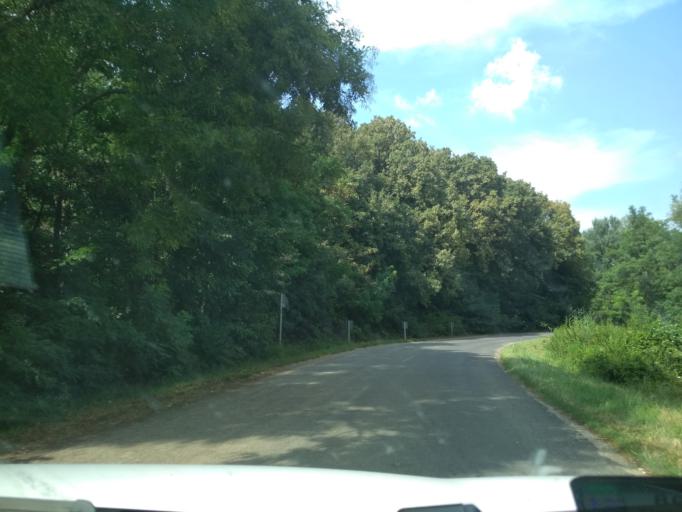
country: HU
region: Jasz-Nagykun-Szolnok
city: Tiszaszolos
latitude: 47.5281
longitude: 20.6932
